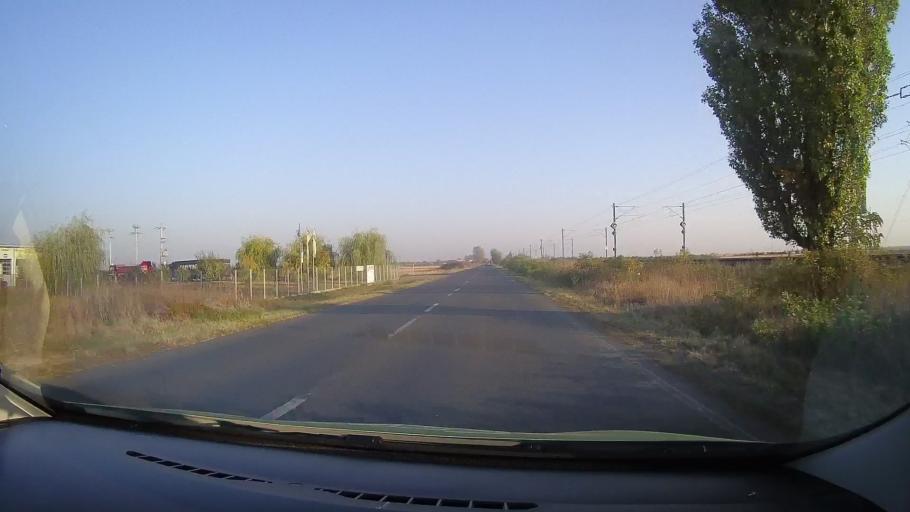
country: RO
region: Arad
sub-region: Comuna Sofronea
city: Sofronea
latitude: 46.2633
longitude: 21.3169
